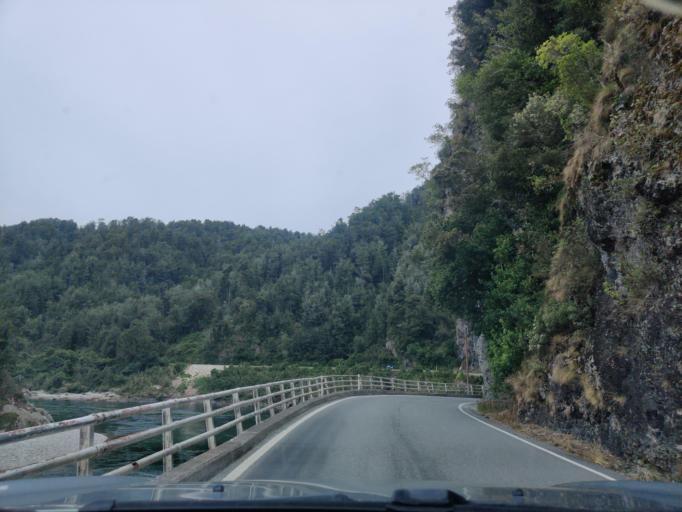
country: NZ
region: West Coast
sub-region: Buller District
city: Westport
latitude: -41.8645
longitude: 171.7787
